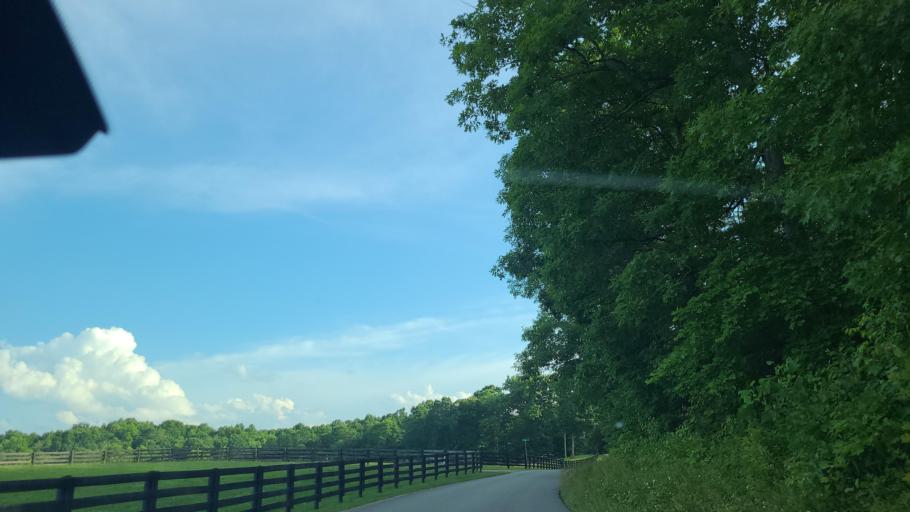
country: US
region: Kentucky
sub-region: Whitley County
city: Corbin
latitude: 36.8862
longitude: -84.2354
